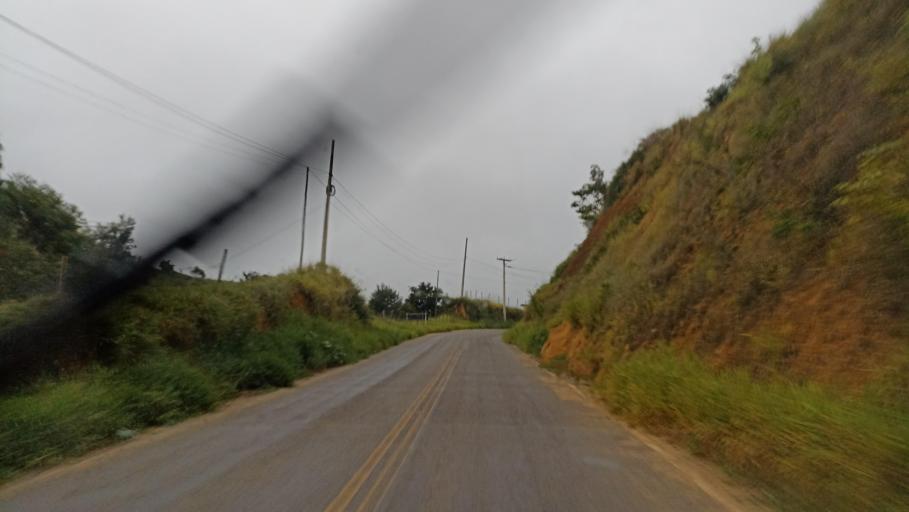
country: BR
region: Bahia
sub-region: Itanhem
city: Itanhem
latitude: -16.7352
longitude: -40.4299
